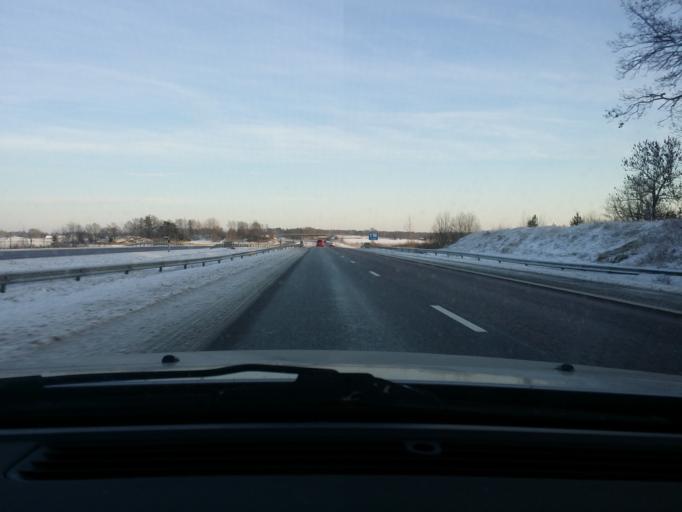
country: SE
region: OErebro
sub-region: Orebro Kommun
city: Hovsta
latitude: 59.3070
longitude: 15.3586
